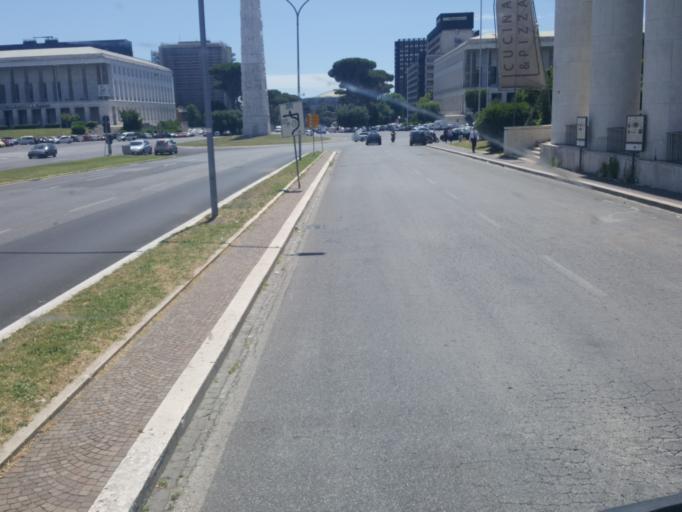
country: IT
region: Latium
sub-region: Citta metropolitana di Roma Capitale
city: Selcetta
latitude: 41.8348
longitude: 12.4713
